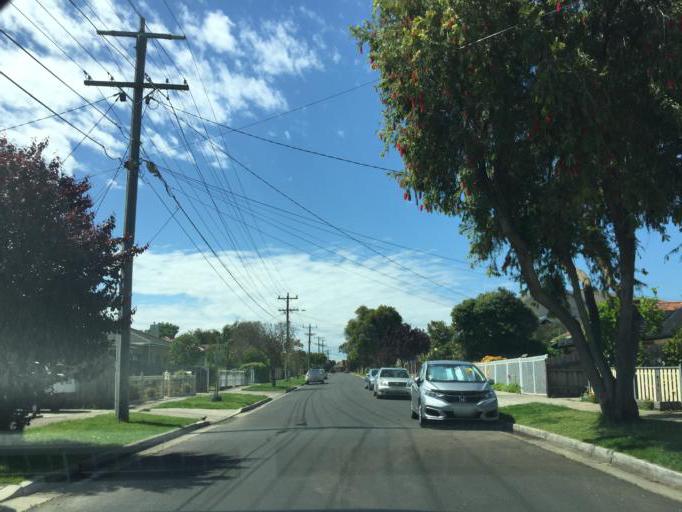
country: AU
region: Victoria
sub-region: Maribyrnong
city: Braybrook
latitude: -37.7881
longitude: 144.8412
